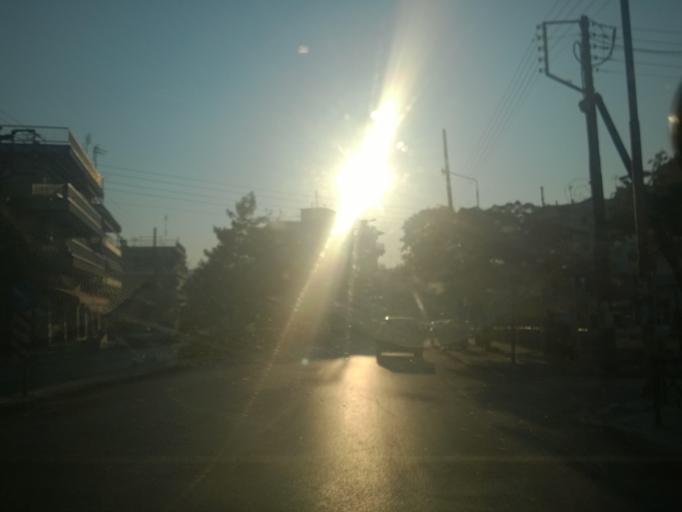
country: GR
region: Central Macedonia
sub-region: Nomos Thessalonikis
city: Stavroupoli
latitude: 40.6662
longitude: 22.9278
